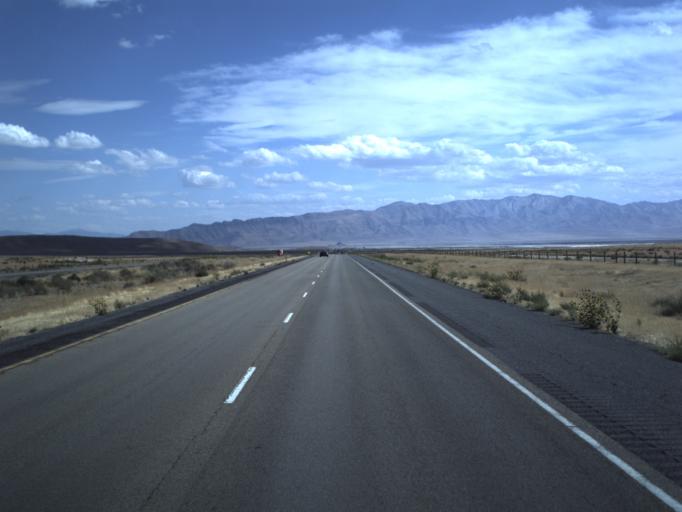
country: US
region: Utah
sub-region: Tooele County
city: Grantsville
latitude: 40.7978
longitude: -112.8457
